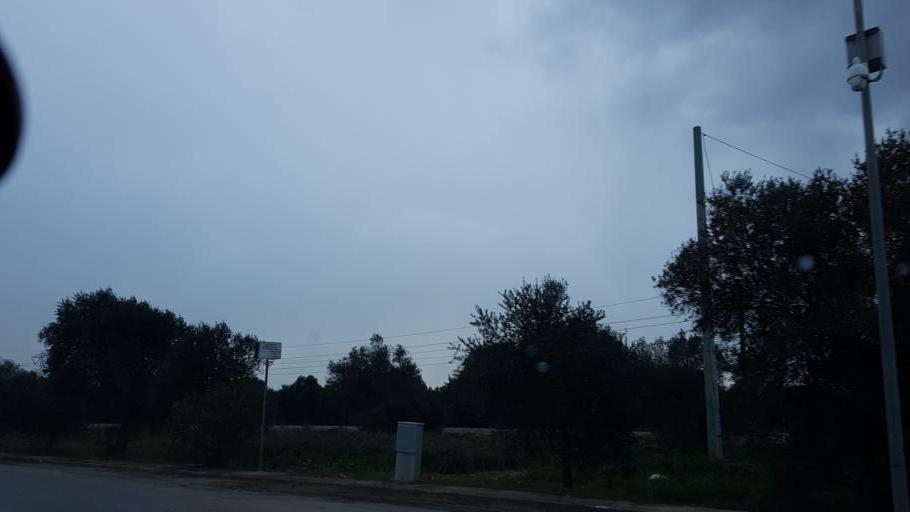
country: IT
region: Apulia
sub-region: Provincia di Brindisi
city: Mesagne
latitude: 40.5821
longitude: 17.8369
